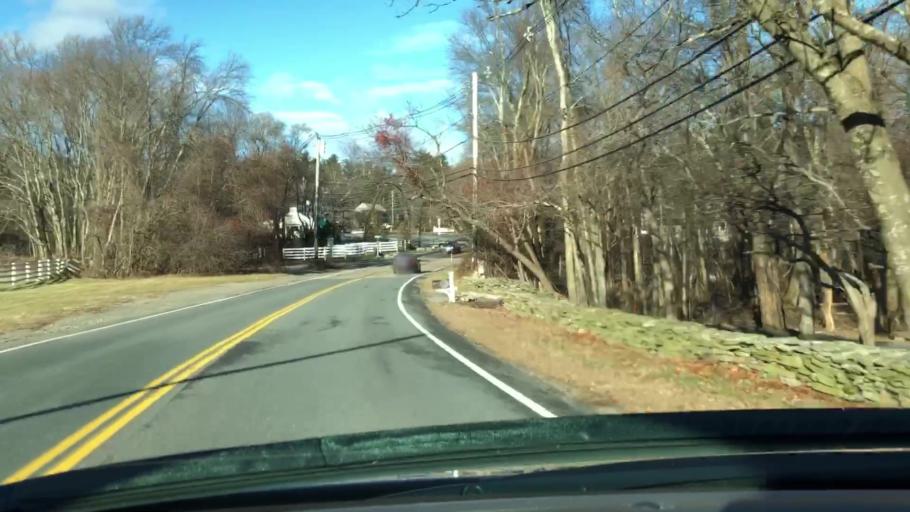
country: US
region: Massachusetts
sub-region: Norfolk County
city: Westwood
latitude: 42.2000
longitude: -71.2499
